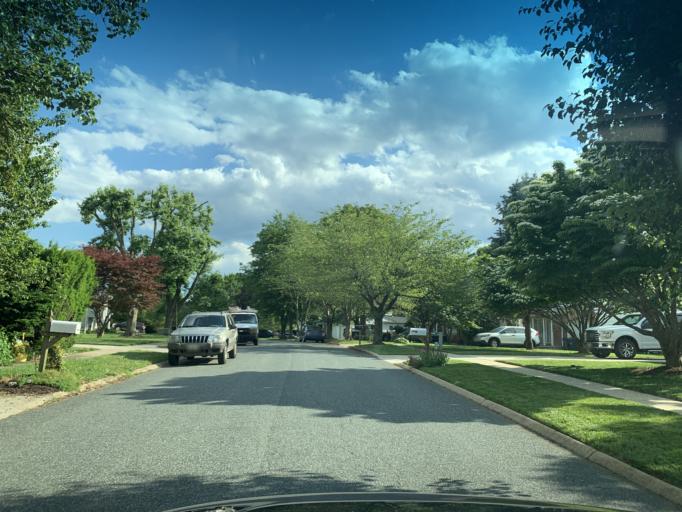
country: US
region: Maryland
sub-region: Harford County
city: Bel Air North
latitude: 39.5467
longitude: -76.3729
